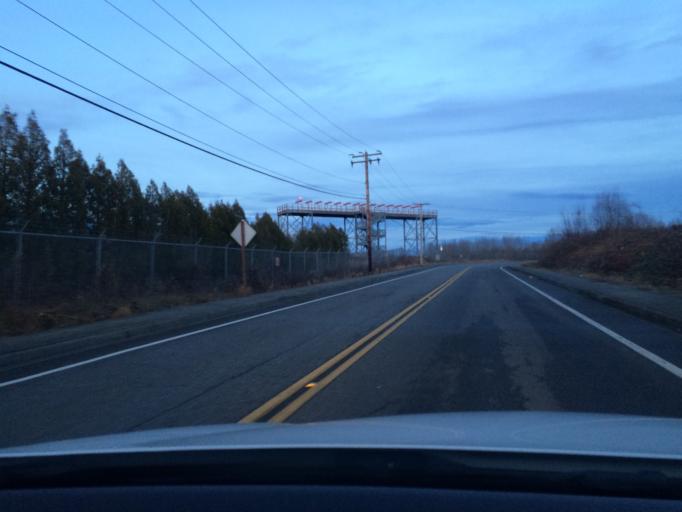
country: US
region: Washington
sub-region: Whatcom County
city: Marietta-Alderwood
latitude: 48.7798
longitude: -122.5383
